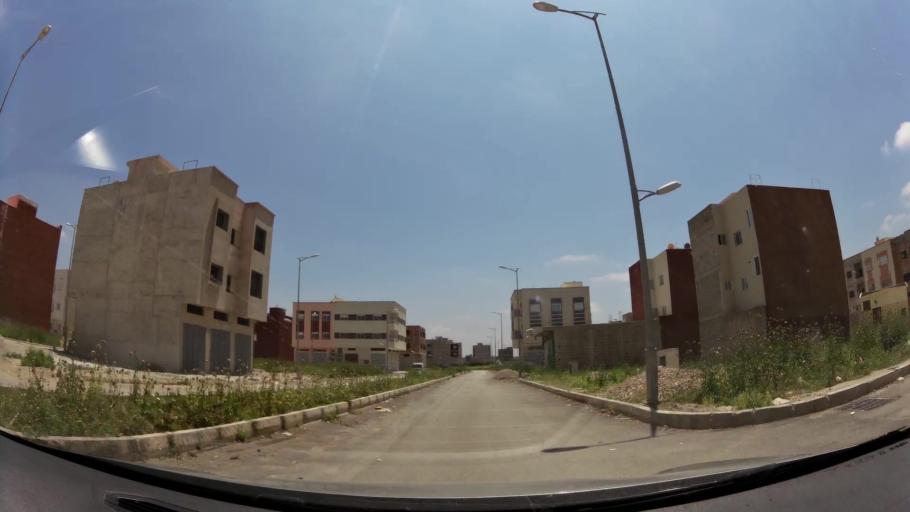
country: MA
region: Fes-Boulemane
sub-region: Fes
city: Fes
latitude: 34.0319
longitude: -5.0544
